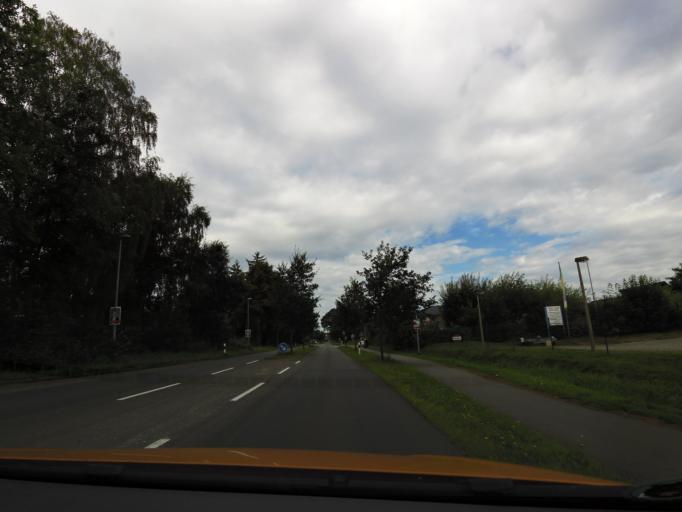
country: DE
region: Lower Saxony
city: Oldenburg
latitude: 53.1664
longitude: 8.1561
